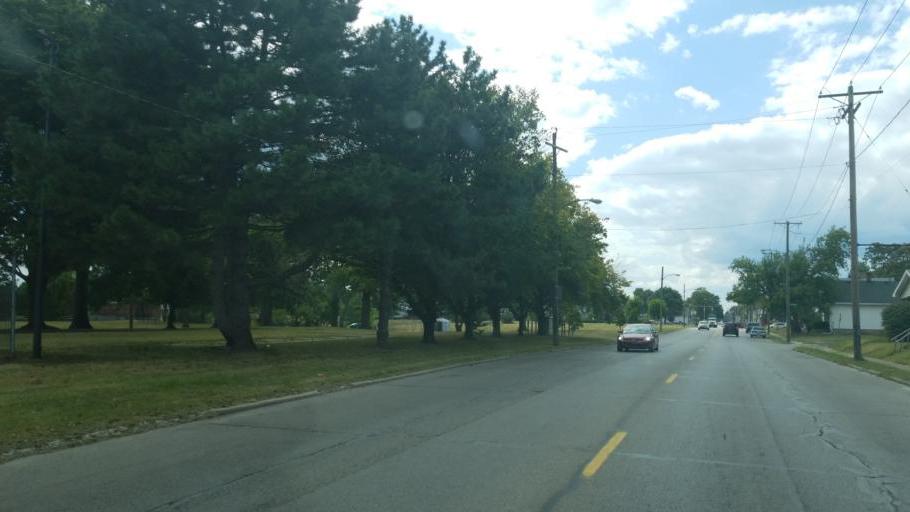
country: US
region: Ohio
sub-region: Lucas County
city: Oregon
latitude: 41.6365
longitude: -83.5076
